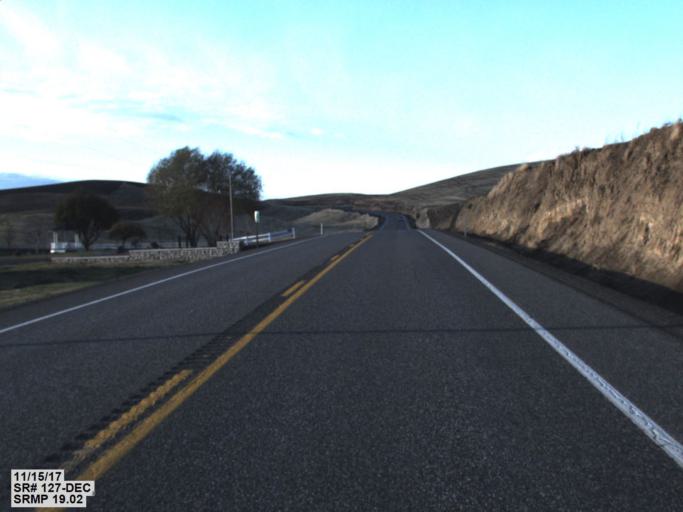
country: US
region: Washington
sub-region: Garfield County
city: Pomeroy
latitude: 46.7302
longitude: -117.7588
